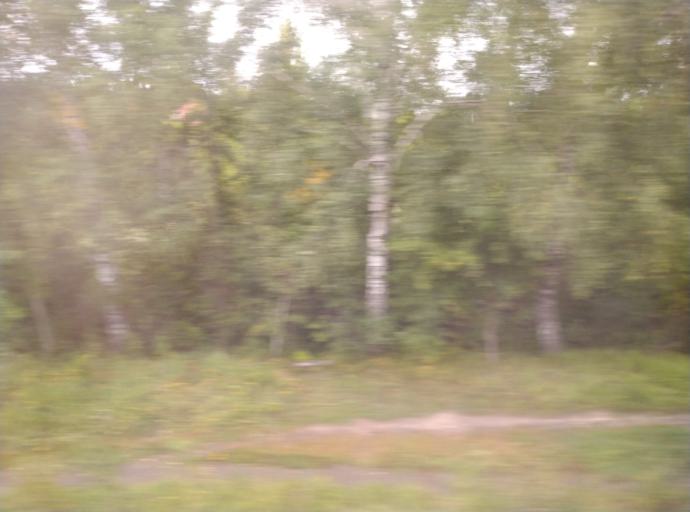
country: RU
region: Kostroma
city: Nerekhta
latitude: 57.4713
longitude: 40.5704
